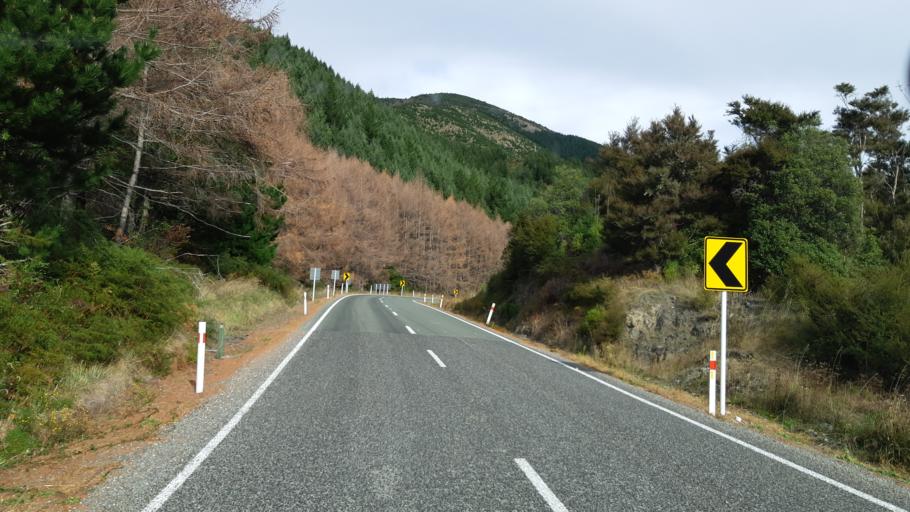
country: NZ
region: Tasman
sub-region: Tasman District
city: Wakefield
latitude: -41.7106
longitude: 173.1145
